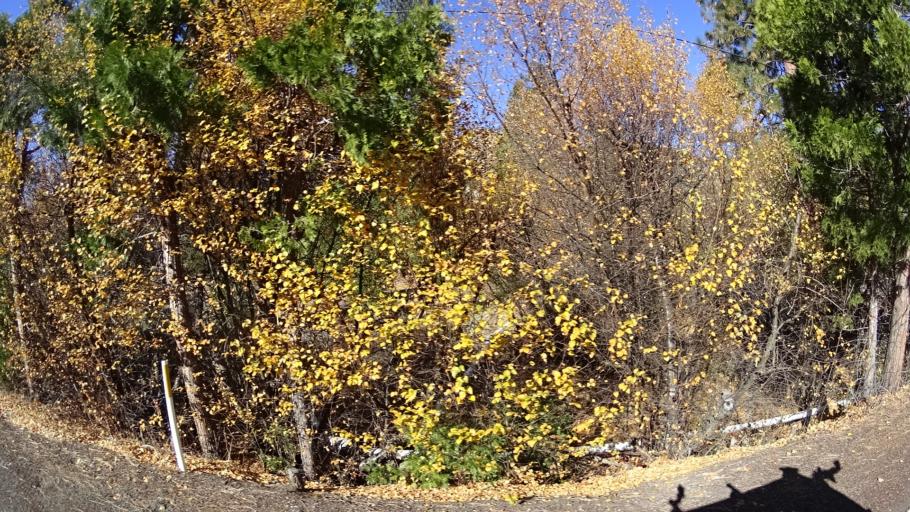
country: US
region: California
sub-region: Siskiyou County
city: Weed
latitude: 41.4739
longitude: -122.5796
